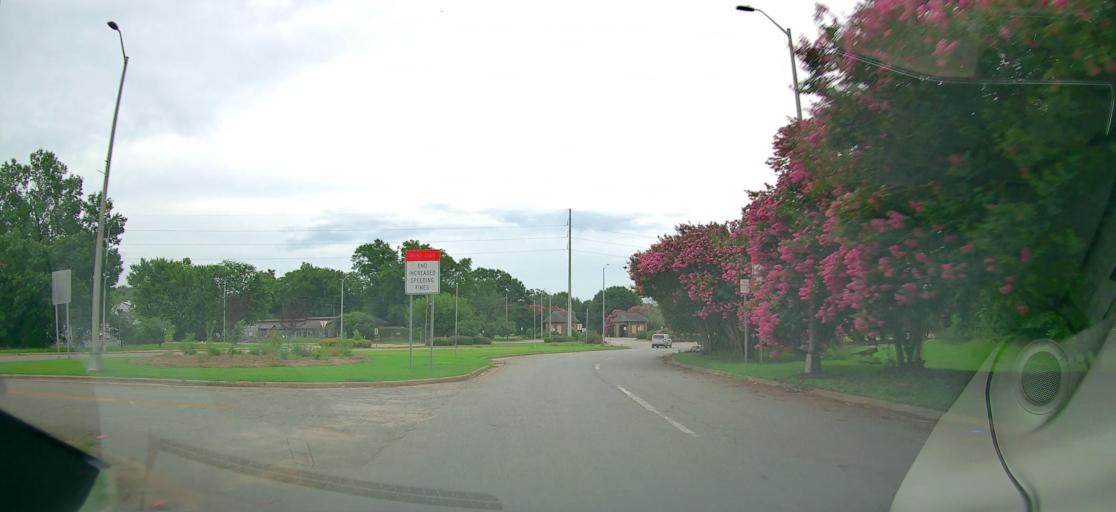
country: US
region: Georgia
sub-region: Bibb County
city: Macon
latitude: 32.8364
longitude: -83.6192
